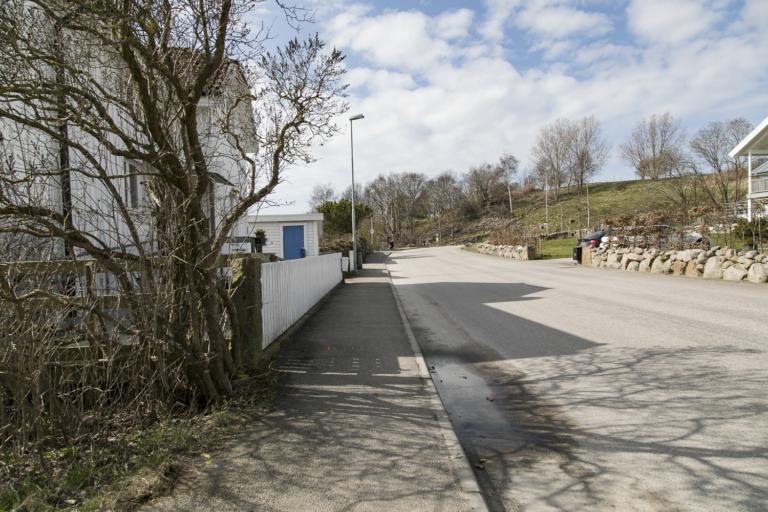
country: SE
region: Halland
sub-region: Varbergs Kommun
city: Varberg
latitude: 57.0906
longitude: 12.2525
